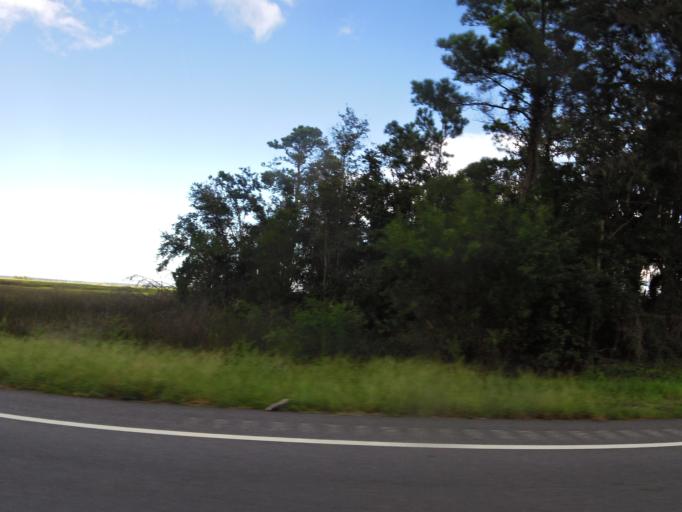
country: US
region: Georgia
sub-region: Glynn County
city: Country Club Estates
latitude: 31.2072
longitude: -81.4668
